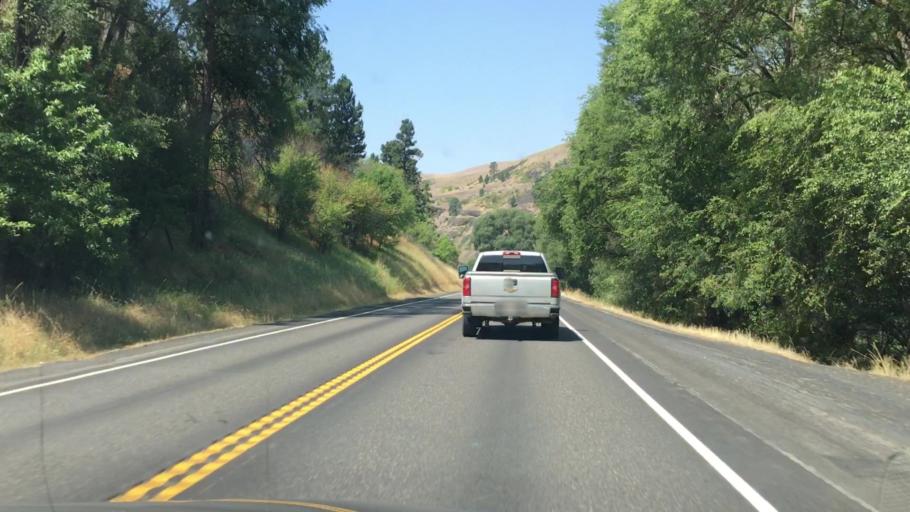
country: US
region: Idaho
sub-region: Nez Perce County
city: Lapwai
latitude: 46.4878
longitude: -116.7427
